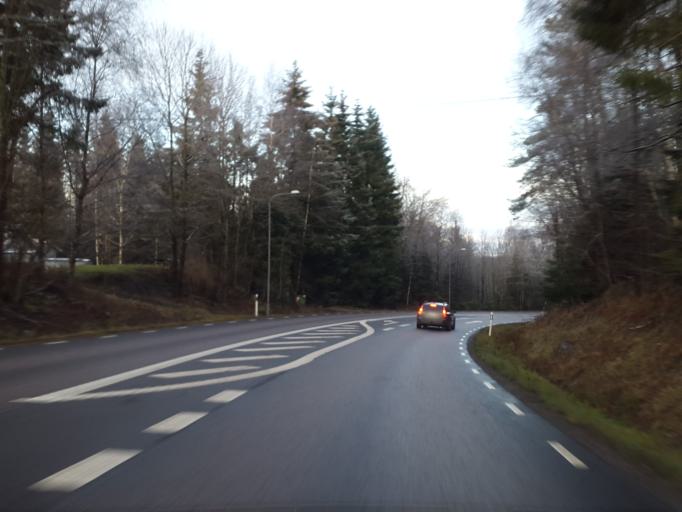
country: SE
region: Vaestra Goetaland
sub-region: Boras Kommun
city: Sjomarken
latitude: 57.7611
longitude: 12.8333
